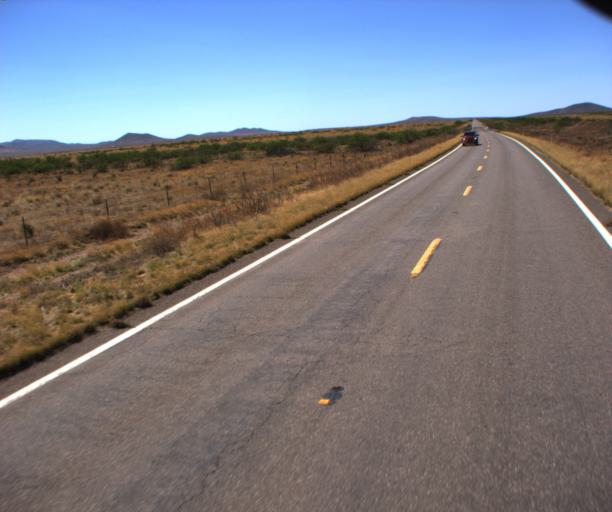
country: US
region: Arizona
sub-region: Cochise County
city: Douglas
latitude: 31.6844
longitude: -109.1371
